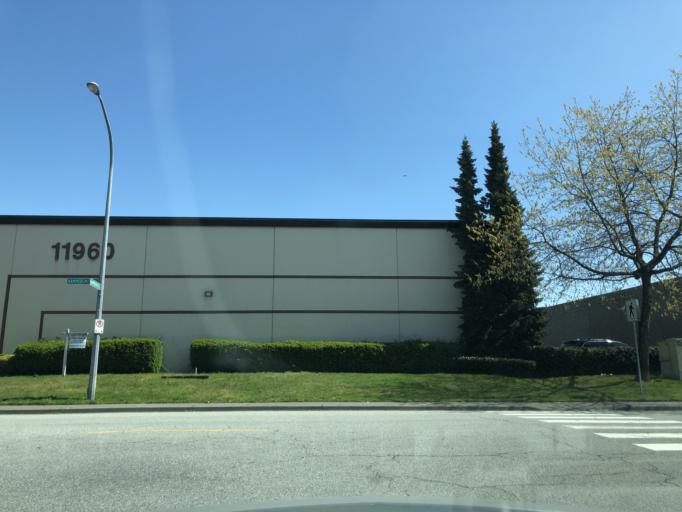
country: CA
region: British Columbia
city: Ladner
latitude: 49.1272
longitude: -123.1007
